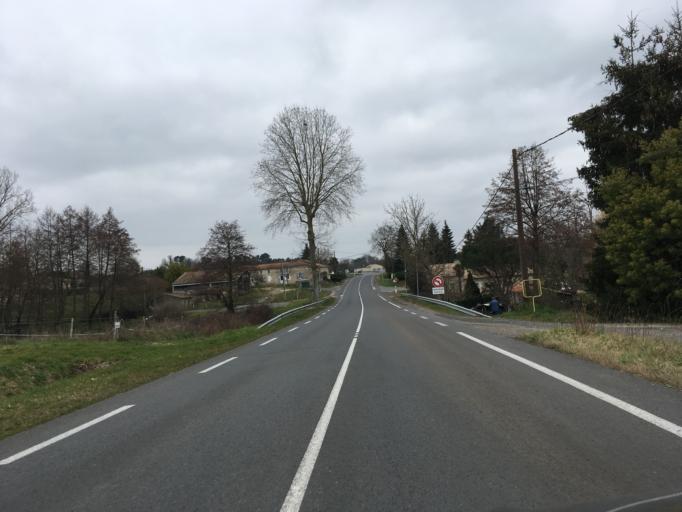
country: FR
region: Aquitaine
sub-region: Departement de la Gironde
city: Saint-Ciers-sur-Gironde
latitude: 45.3096
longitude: -0.5750
